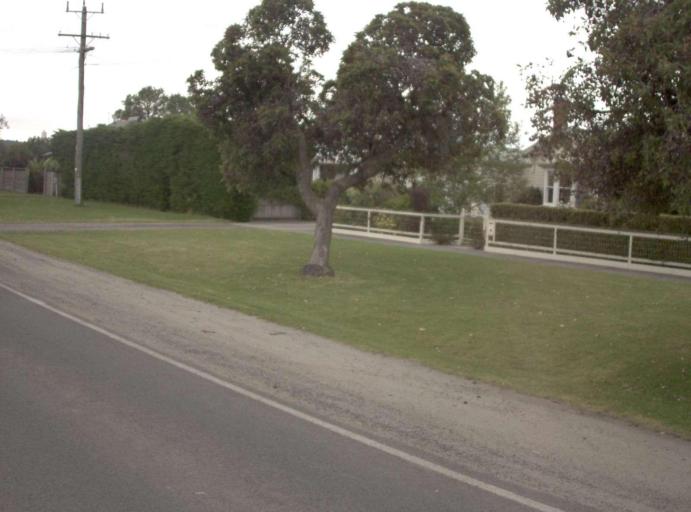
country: AU
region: Victoria
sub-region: Latrobe
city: Traralgon
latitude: -38.5551
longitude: 146.6787
